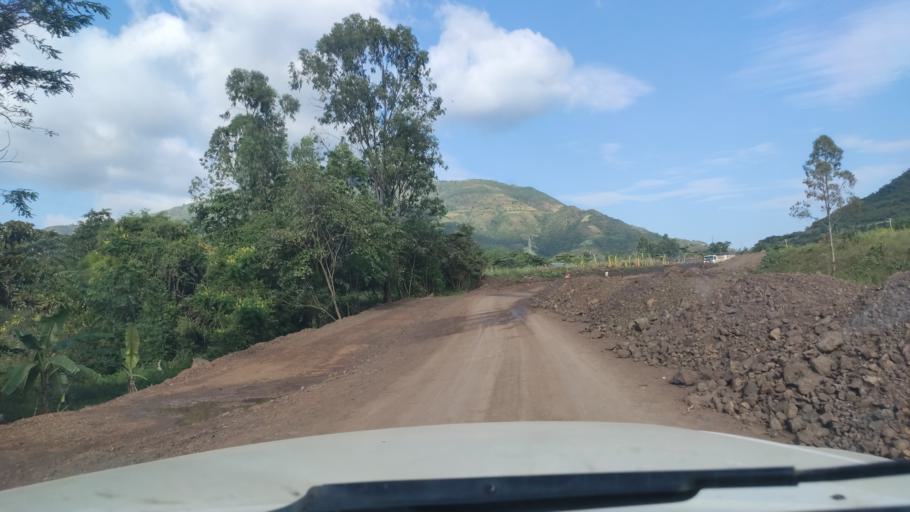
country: ET
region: Southern Nations, Nationalities, and People's Region
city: Arba Minch'
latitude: 6.4262
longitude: 37.3314
